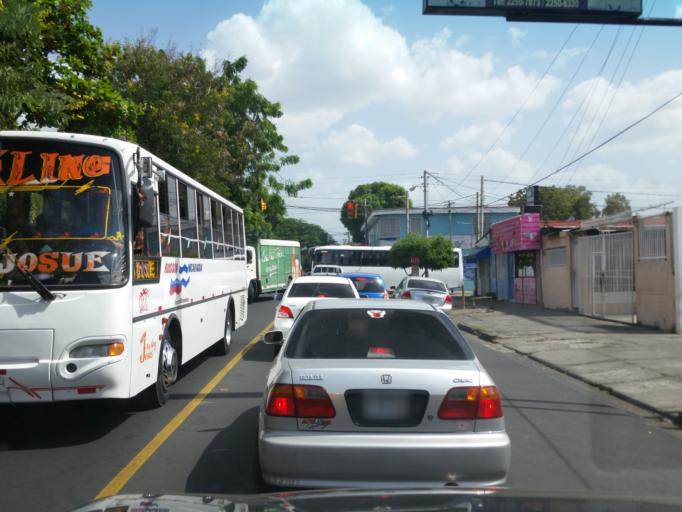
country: NI
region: Managua
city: Managua
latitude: 12.1426
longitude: -86.2512
